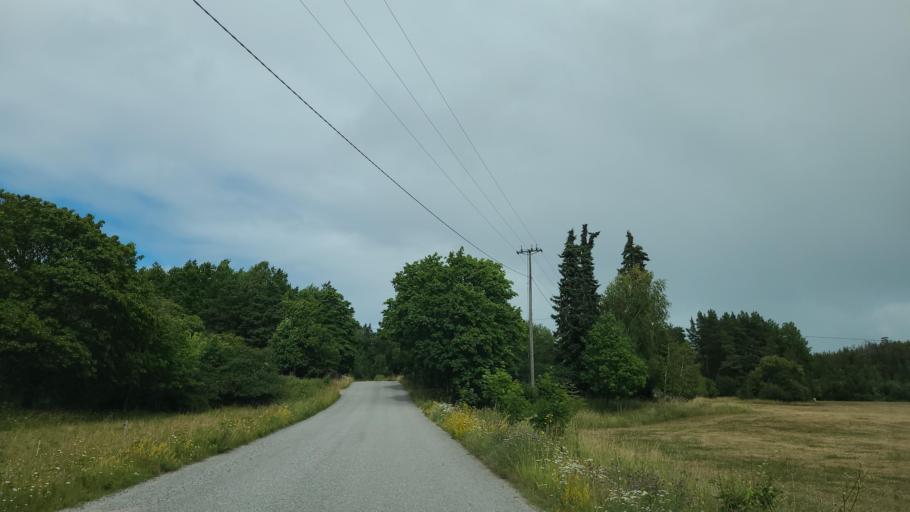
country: FI
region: Varsinais-Suomi
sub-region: Aboland-Turunmaa
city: Nagu
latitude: 60.1680
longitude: 21.9811
